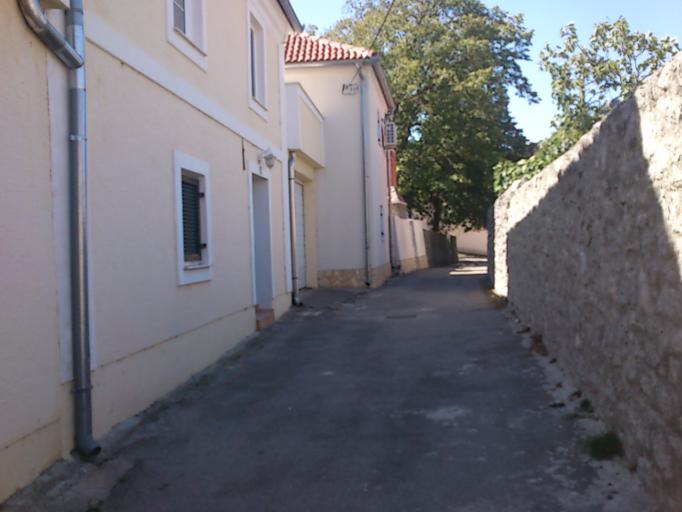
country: HR
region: Licko-Senjska
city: Senj
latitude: 44.9291
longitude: 14.9207
